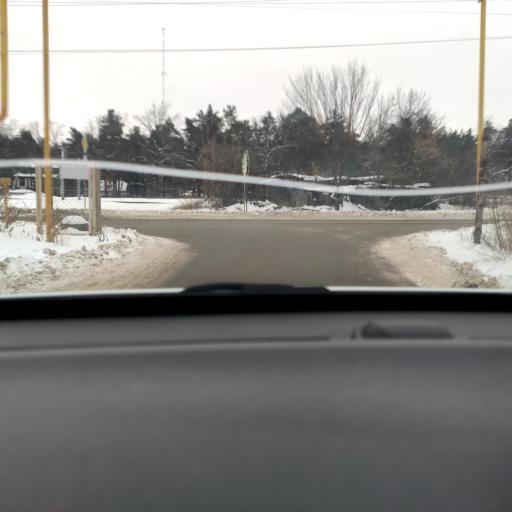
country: RU
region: Voronezj
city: Somovo
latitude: 51.7473
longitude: 39.3802
